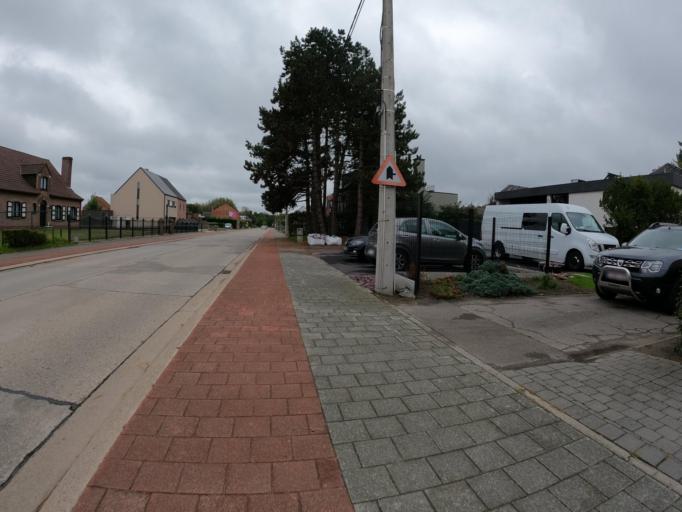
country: BE
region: Flanders
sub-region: Provincie Vlaams-Brabant
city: Begijnendijk
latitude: 51.0273
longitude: 4.7547
